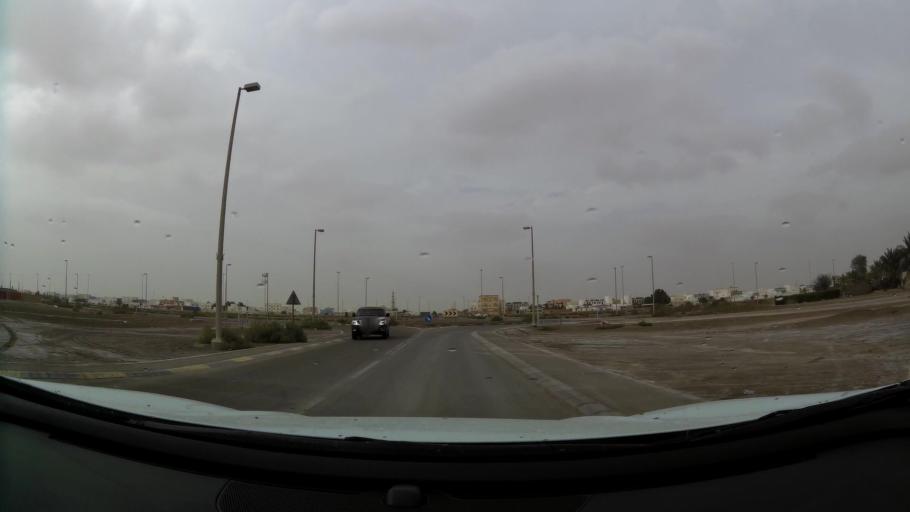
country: AE
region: Abu Dhabi
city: Abu Dhabi
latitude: 24.3587
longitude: 54.6597
